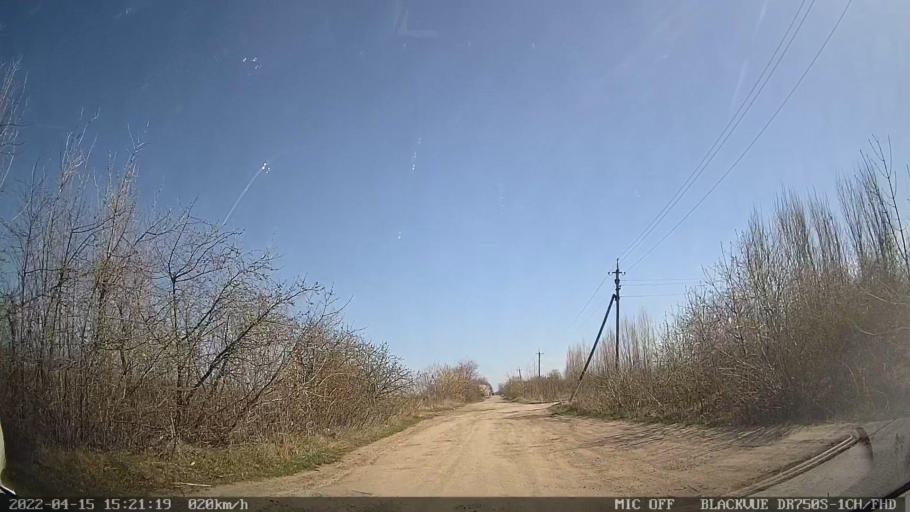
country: MD
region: Raionul Ocnita
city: Otaci
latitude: 48.3839
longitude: 27.9102
